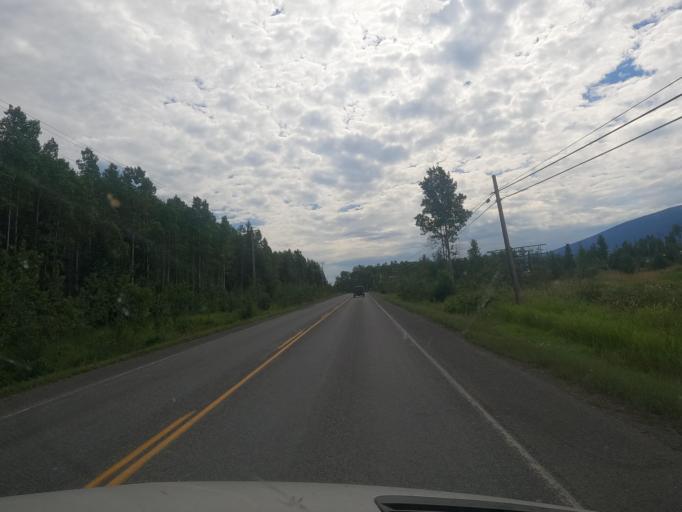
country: CA
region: British Columbia
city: Smithers
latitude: 54.8563
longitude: -127.2261
